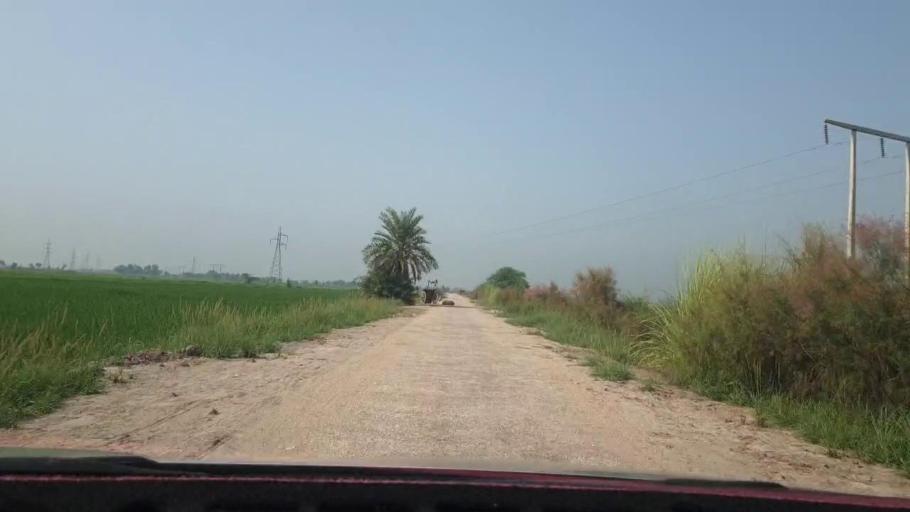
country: PK
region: Sindh
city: Nasirabad
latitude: 27.4259
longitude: 67.9427
